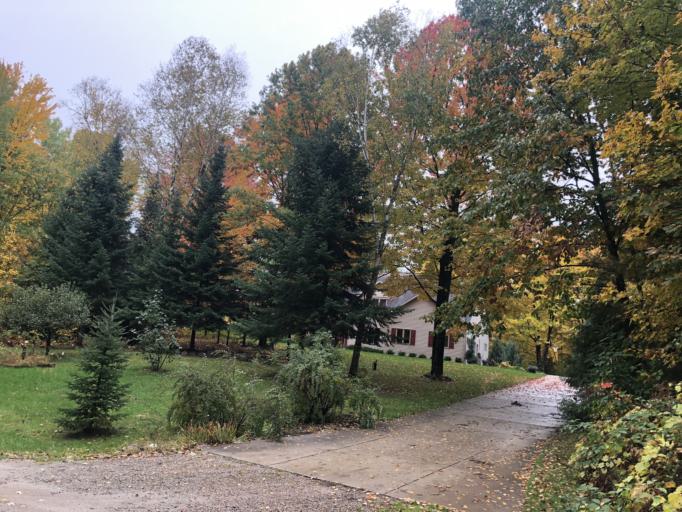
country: US
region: Wisconsin
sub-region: Oconto County
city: Oconto Falls
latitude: 44.8130
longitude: -88.0606
